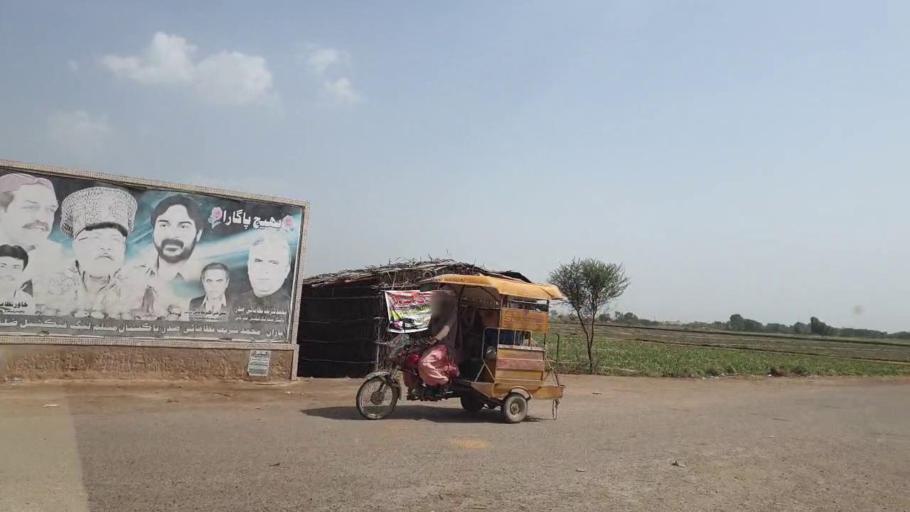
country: PK
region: Sindh
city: Tando Ghulam Ali
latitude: 25.0754
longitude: 68.8228
